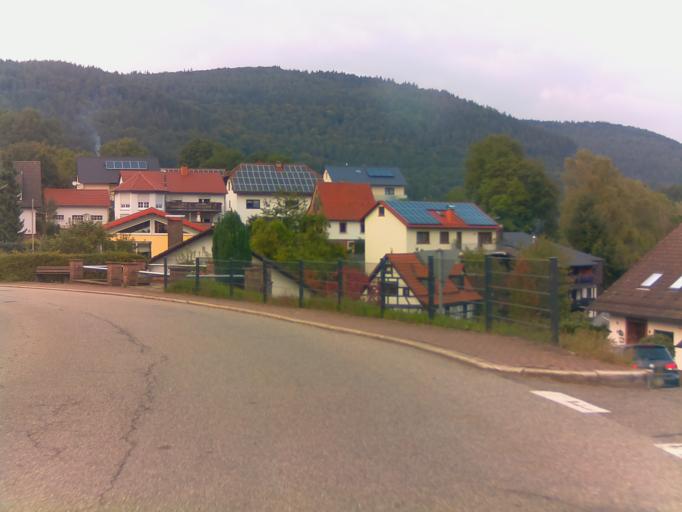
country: DE
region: Baden-Wuerttemberg
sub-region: Karlsruhe Region
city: Heddesbach
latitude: 49.4815
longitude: 8.8279
